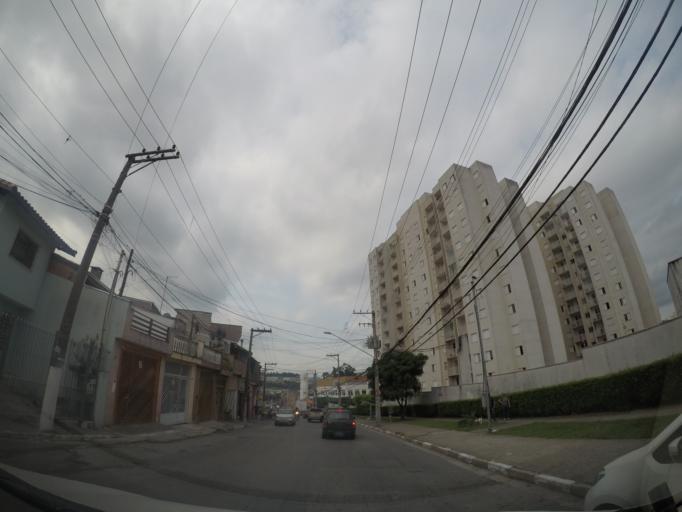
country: BR
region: Sao Paulo
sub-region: Guarulhos
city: Guarulhos
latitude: -23.4298
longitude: -46.5088
